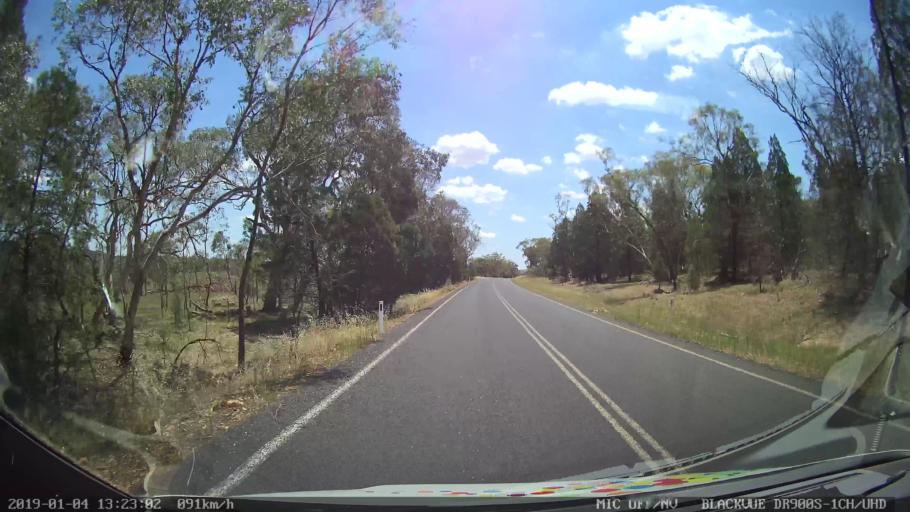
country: AU
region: New South Wales
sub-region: Parkes
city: Peak Hill
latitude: -32.7231
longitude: 148.5580
